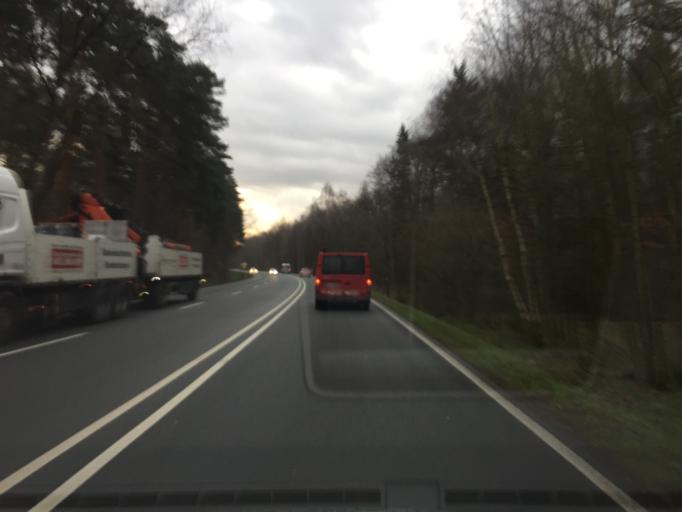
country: DE
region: Lower Saxony
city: Gross Munzel
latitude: 52.4131
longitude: 9.5001
